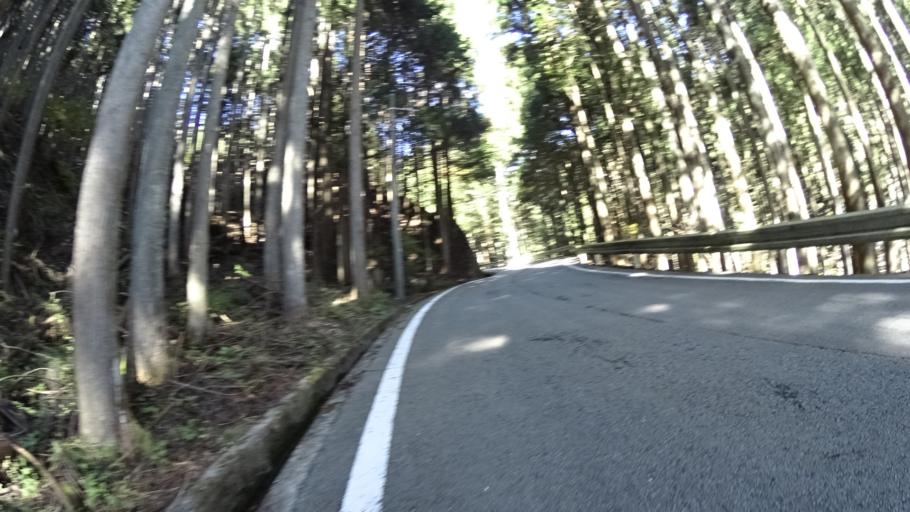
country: JP
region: Yamanashi
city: Otsuki
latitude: 35.7671
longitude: 138.9342
